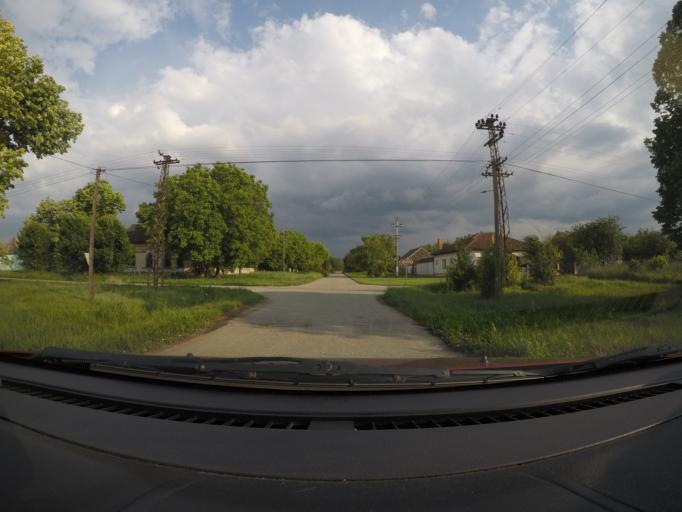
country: RS
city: Debeljaca
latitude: 45.0663
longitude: 20.6001
